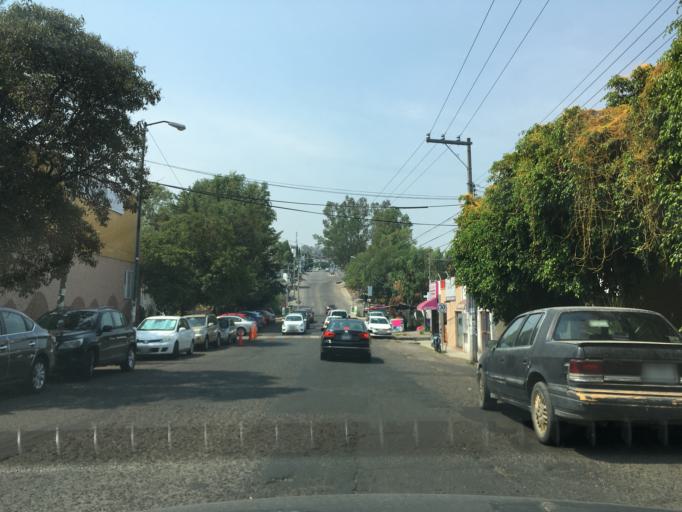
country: MX
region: Michoacan
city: Morelia
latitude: 19.6735
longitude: -101.2007
